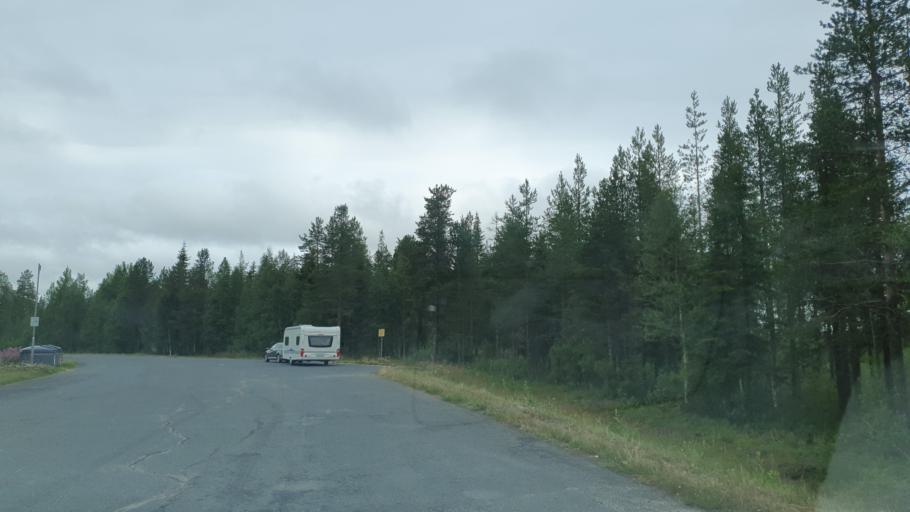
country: FI
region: Lapland
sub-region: Pohjois-Lappi
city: Sodankylae
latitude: 67.4236
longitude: 26.4408
